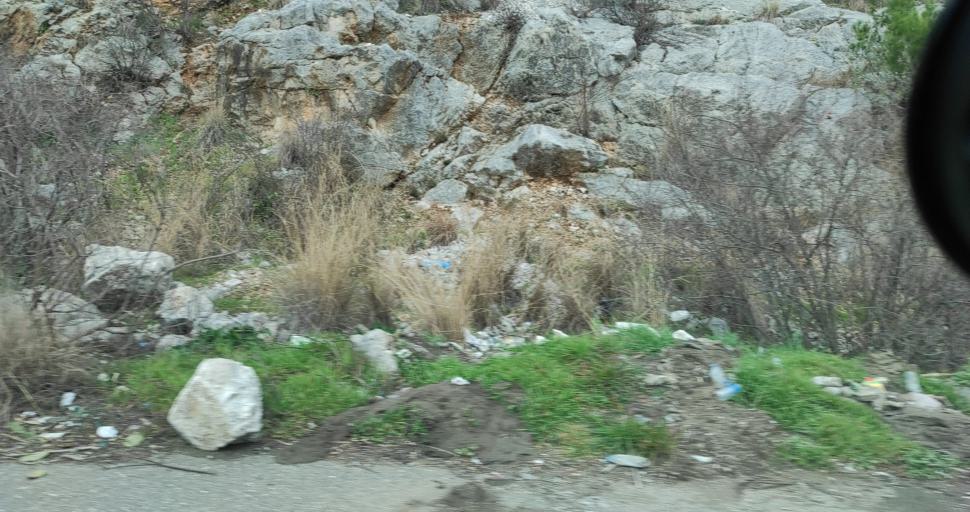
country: AL
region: Lezhe
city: Shengjin
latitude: 41.8063
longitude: 19.6096
